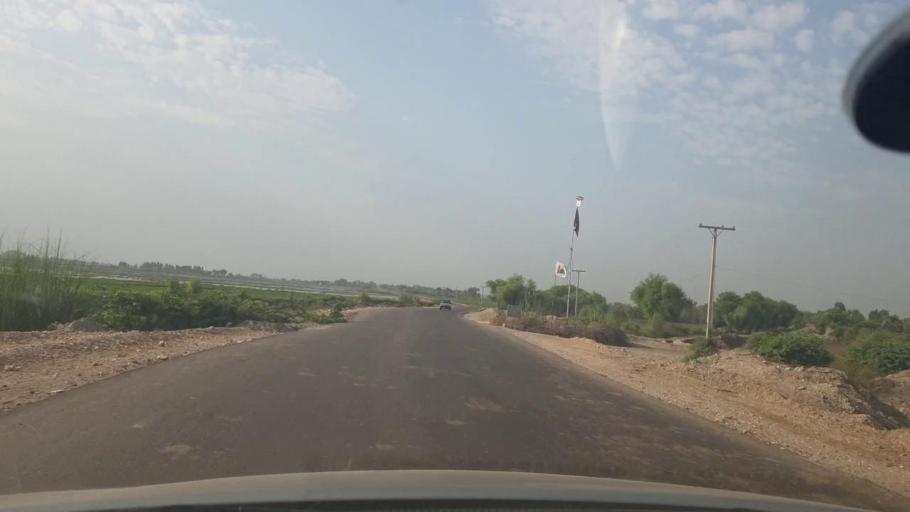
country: PK
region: Sindh
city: Jacobabad
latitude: 28.1246
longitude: 68.3283
